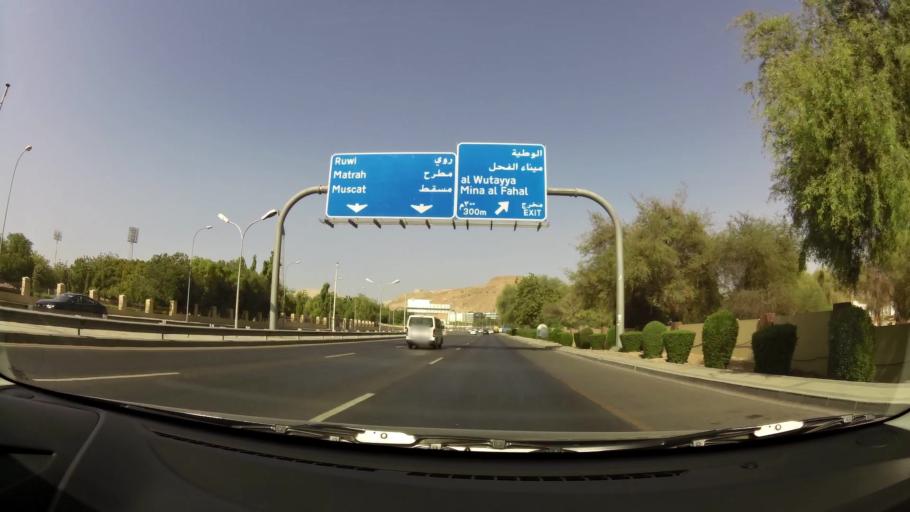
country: OM
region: Muhafazat Masqat
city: Muscat
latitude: 23.6068
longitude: 58.5056
